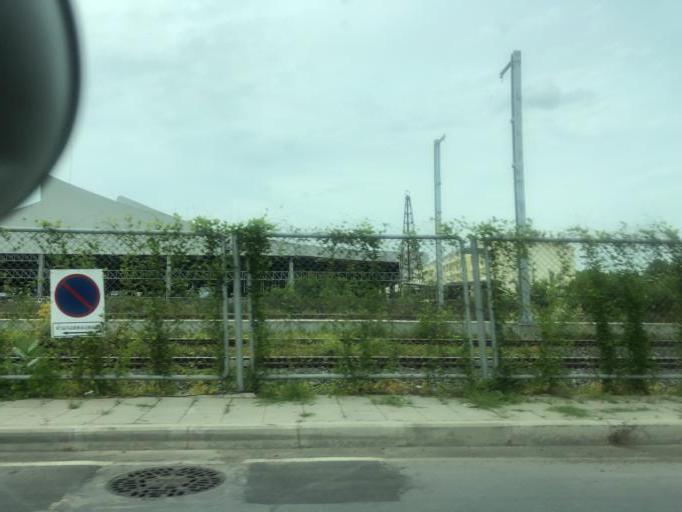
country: TH
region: Bangkok
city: Don Mueang
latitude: 13.9557
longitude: 100.6063
